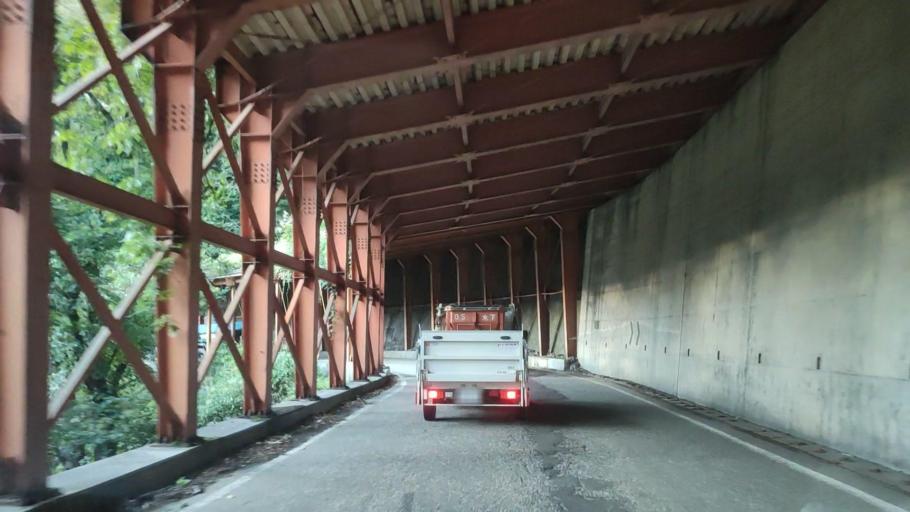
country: JP
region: Toyama
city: Nanto-shi
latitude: 36.5426
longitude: 137.0083
